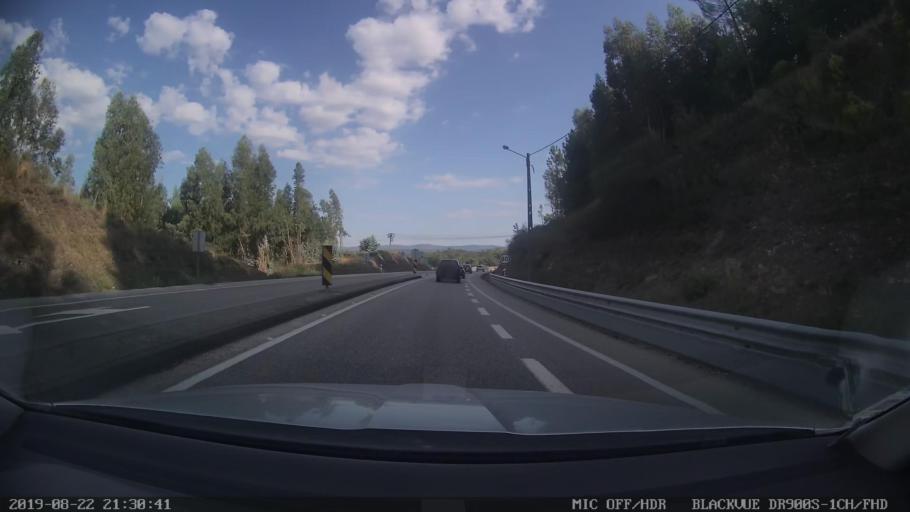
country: PT
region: Leiria
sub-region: Pedrogao Grande
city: Pedrogao Grande
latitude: 39.9117
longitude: -8.1533
